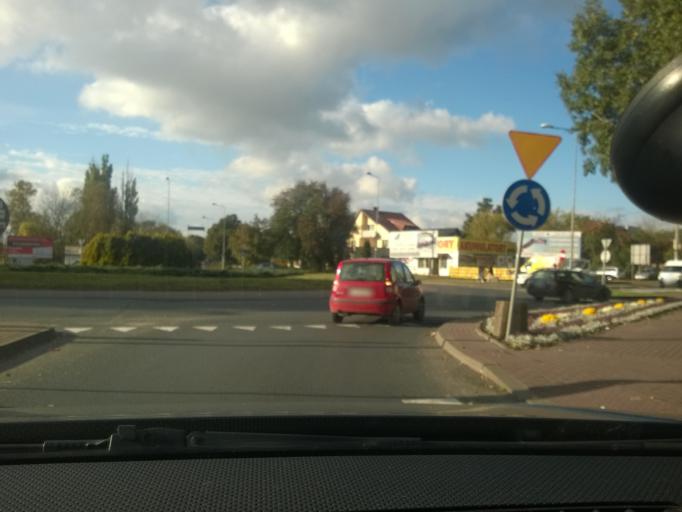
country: PL
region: Masovian Voivodeship
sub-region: Powiat pruszkowski
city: Pruszkow
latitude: 52.1723
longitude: 20.8035
